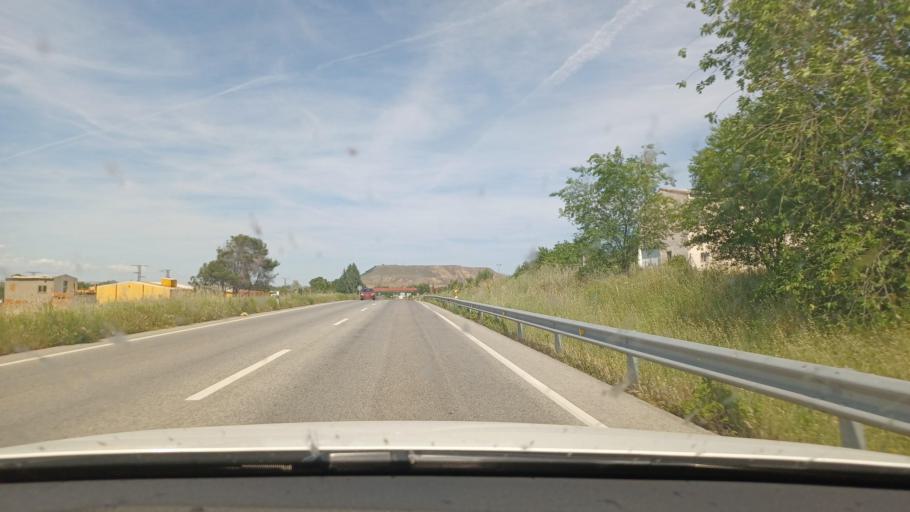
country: ES
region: Madrid
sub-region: Provincia de Madrid
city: Torrejon de Ardoz
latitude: 40.4262
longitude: -3.4522
